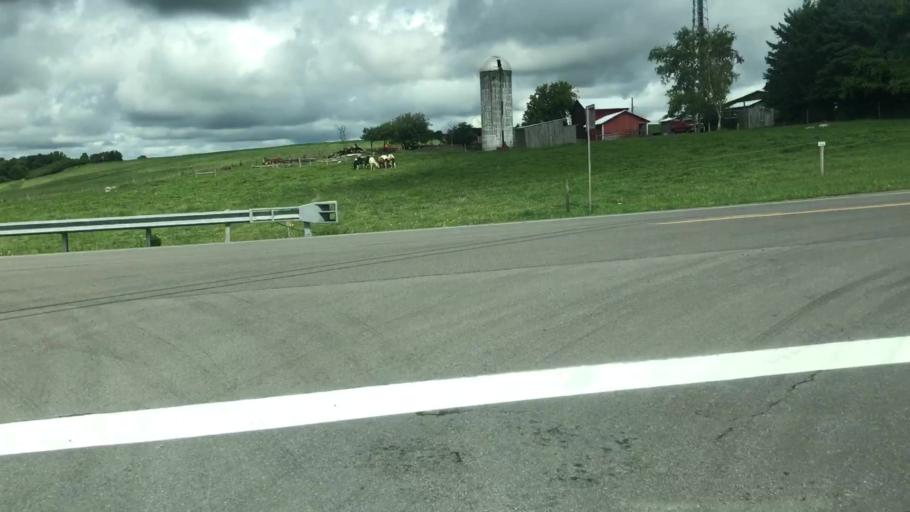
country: US
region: New York
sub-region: Onondaga County
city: Skaneateles
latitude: 42.9426
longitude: -76.4713
